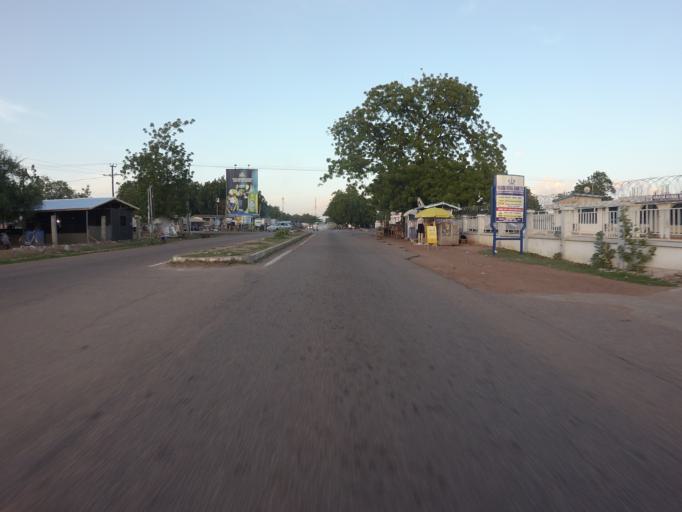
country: GH
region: Upper East
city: Navrongo
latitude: 10.8963
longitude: -1.0904
